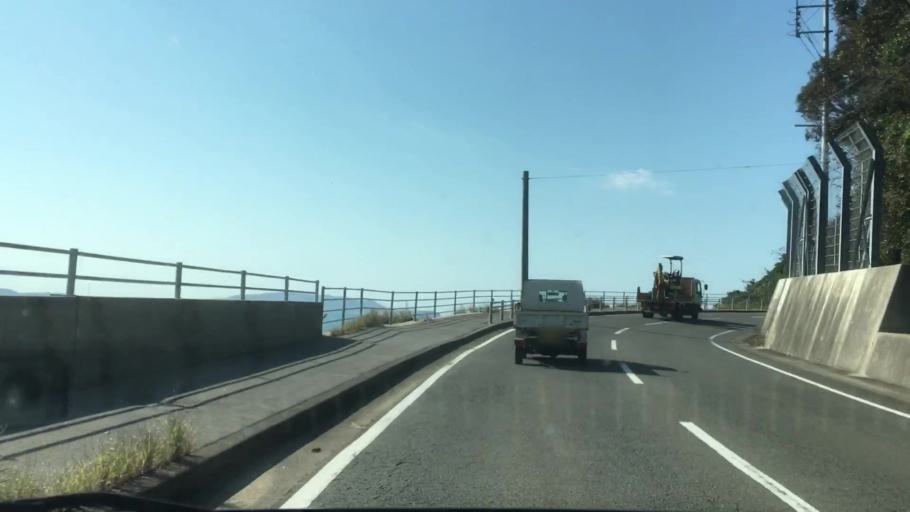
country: JP
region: Nagasaki
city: Sasebo
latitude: 33.0258
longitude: 129.6009
